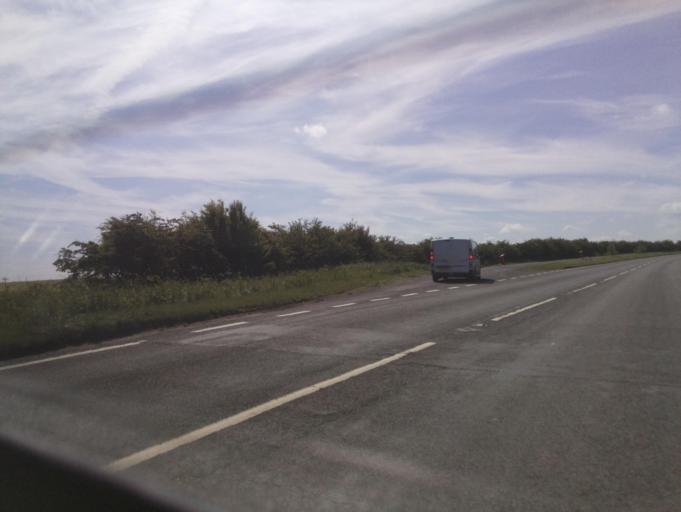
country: GB
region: England
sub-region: North Lincolnshire
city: Manton
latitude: 53.5155
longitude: -0.5799
